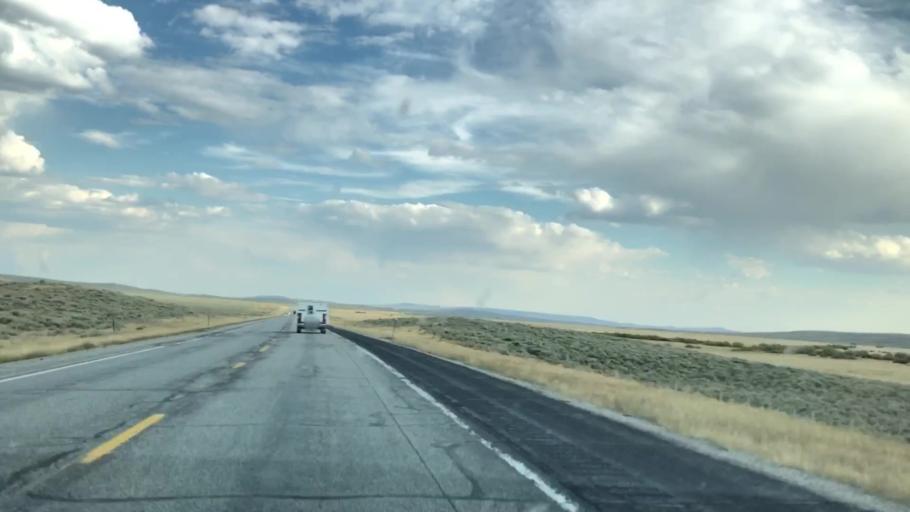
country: US
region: Wyoming
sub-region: Sublette County
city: Pinedale
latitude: 43.0463
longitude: -110.1472
